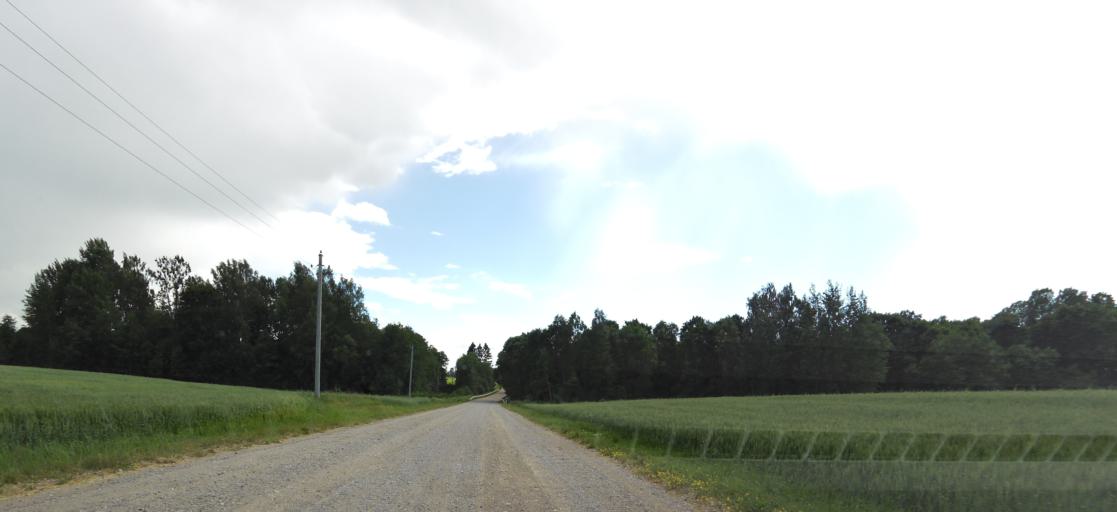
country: LT
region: Panevezys
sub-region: Birzai
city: Birzai
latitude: 56.3528
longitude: 24.6324
